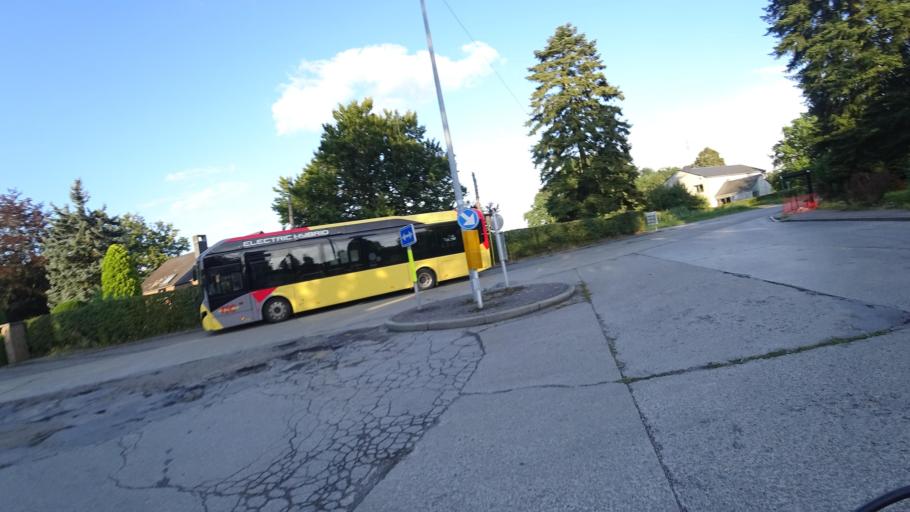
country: BE
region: Wallonia
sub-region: Province de Namur
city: Namur
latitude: 50.4819
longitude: 4.8259
